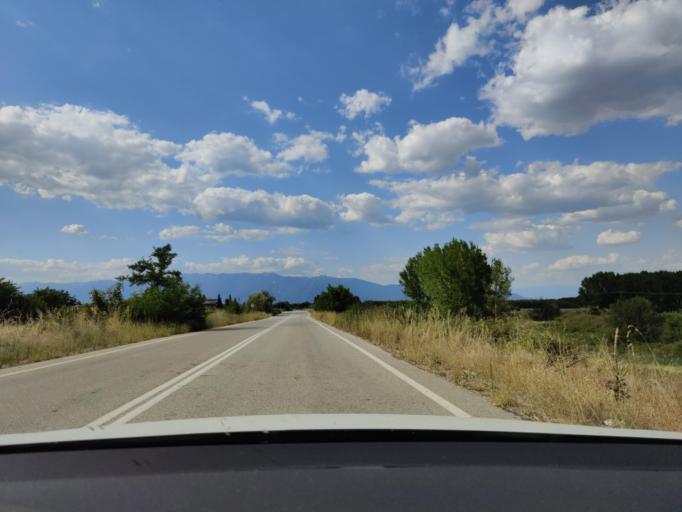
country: GR
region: Central Macedonia
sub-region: Nomos Serron
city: Strymoniko
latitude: 41.1039
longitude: 23.2672
